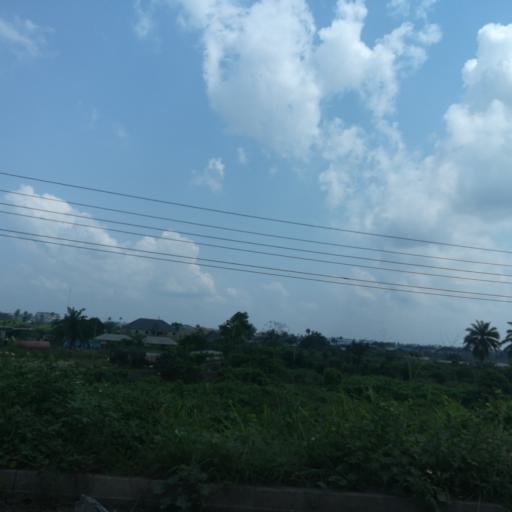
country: NG
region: Rivers
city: Port Harcourt
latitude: 4.8444
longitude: 7.0779
